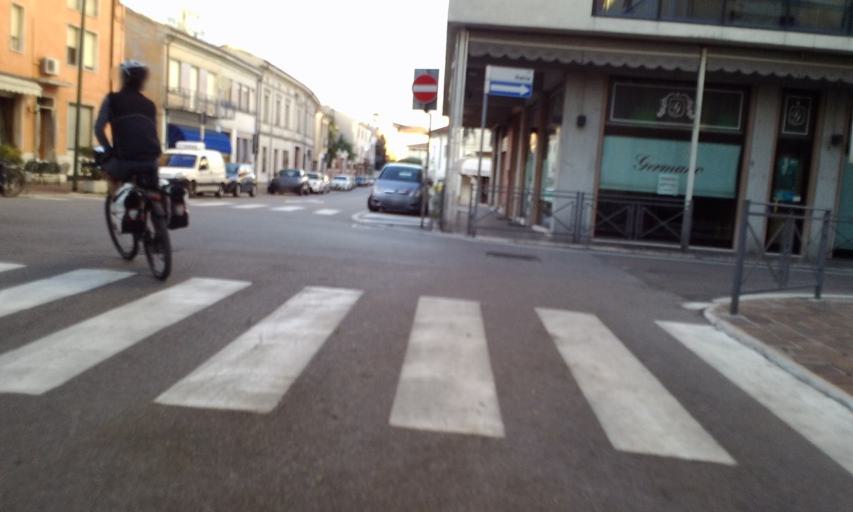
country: IT
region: Lombardy
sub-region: Provincia di Mantova
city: Ostiglia
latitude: 45.0646
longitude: 11.1340
